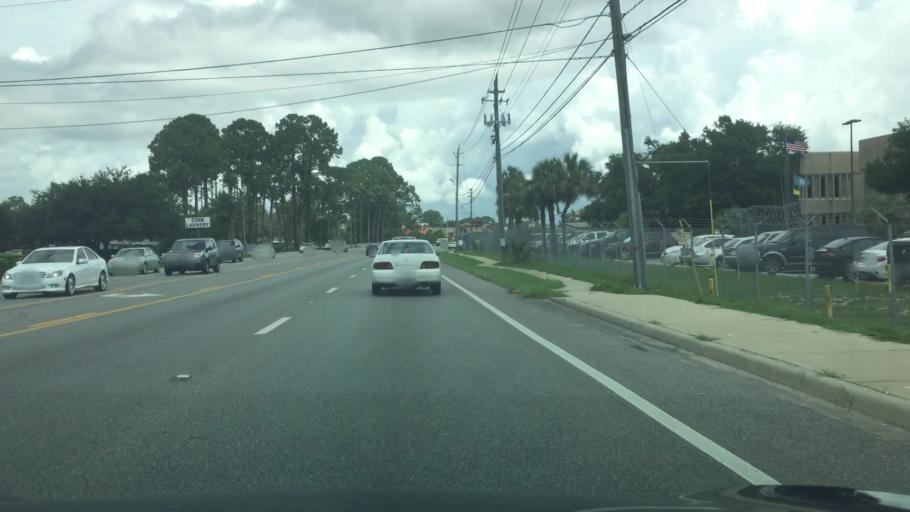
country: US
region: Florida
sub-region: Bay County
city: Upper Grand Lagoon
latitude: 30.1708
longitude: -85.7588
